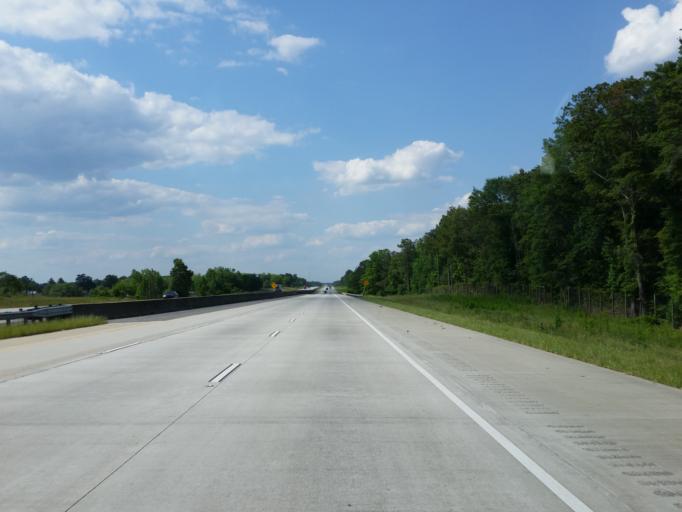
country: US
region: Georgia
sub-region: Dooly County
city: Unadilla
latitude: 32.2988
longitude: -83.7610
